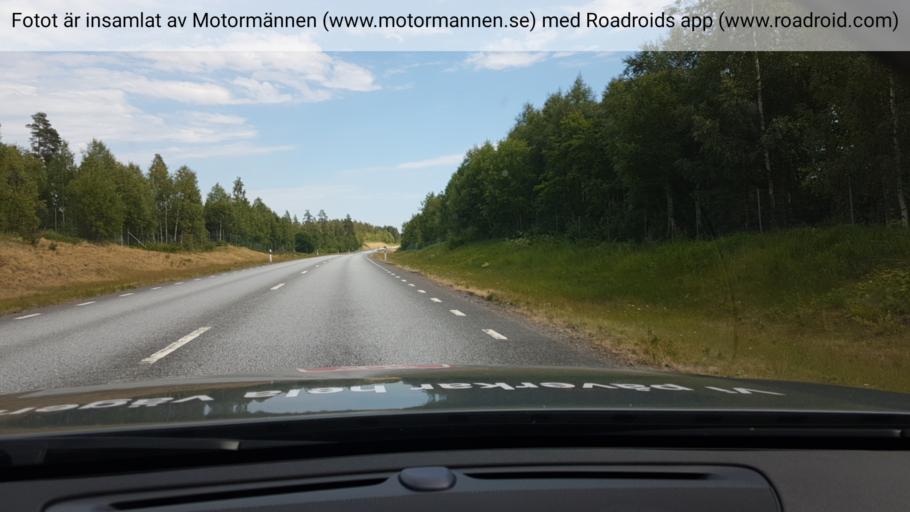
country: SE
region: Uppsala
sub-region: Osthammars Kommun
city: OEsthammar
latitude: 60.1734
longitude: 18.3587
